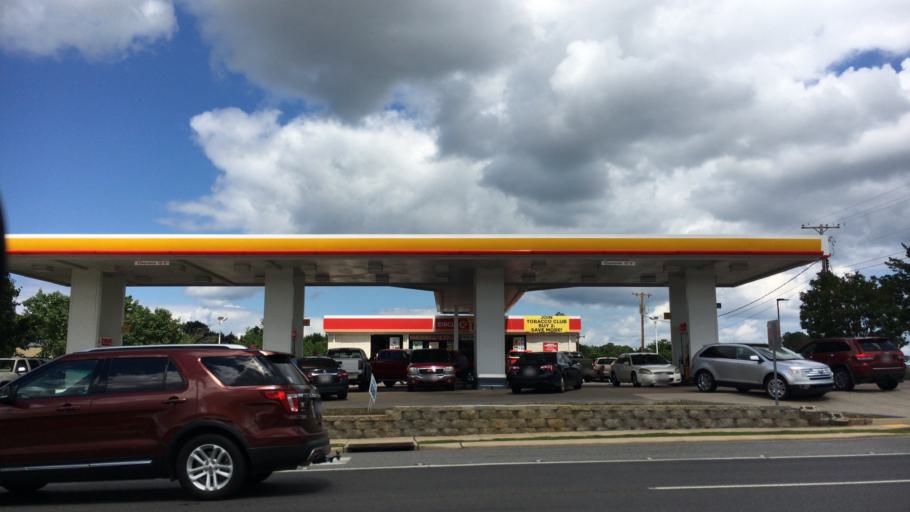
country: US
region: Louisiana
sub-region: Lincoln Parish
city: Ruston
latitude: 32.5442
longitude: -92.6396
